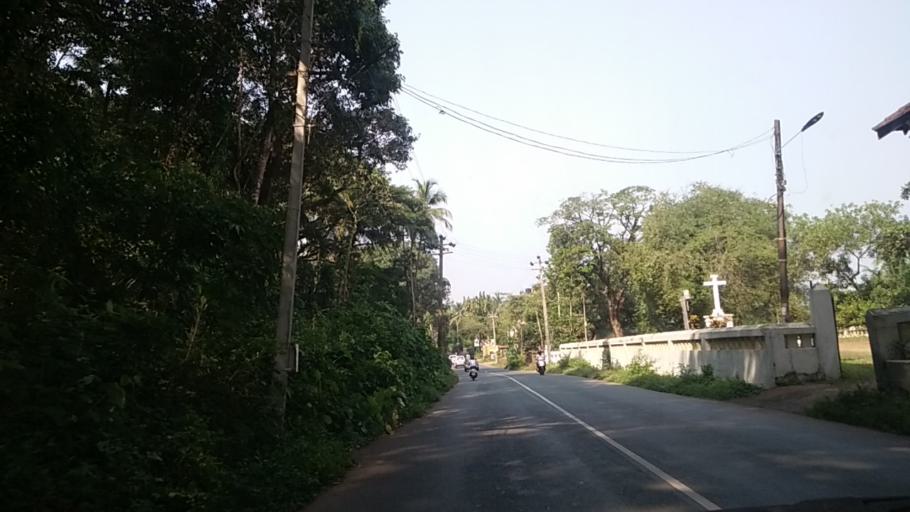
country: IN
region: Goa
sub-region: North Goa
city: Bambolim
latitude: 15.5002
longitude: 73.8971
